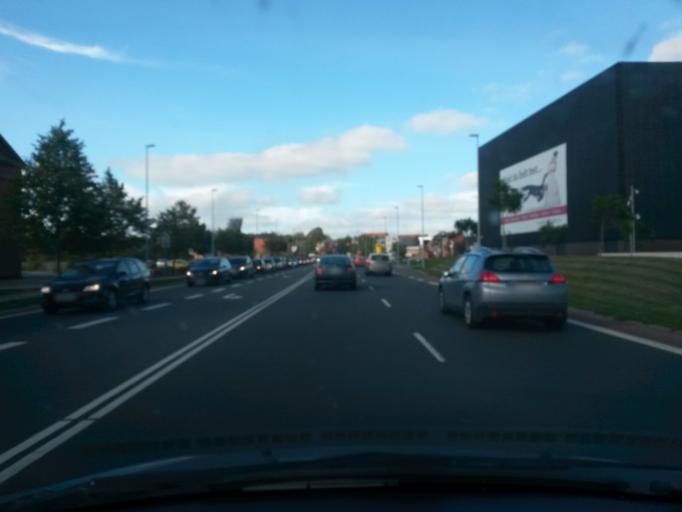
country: DK
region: Central Jutland
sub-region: Holstebro Kommune
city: Holstebro
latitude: 56.3558
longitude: 8.6152
